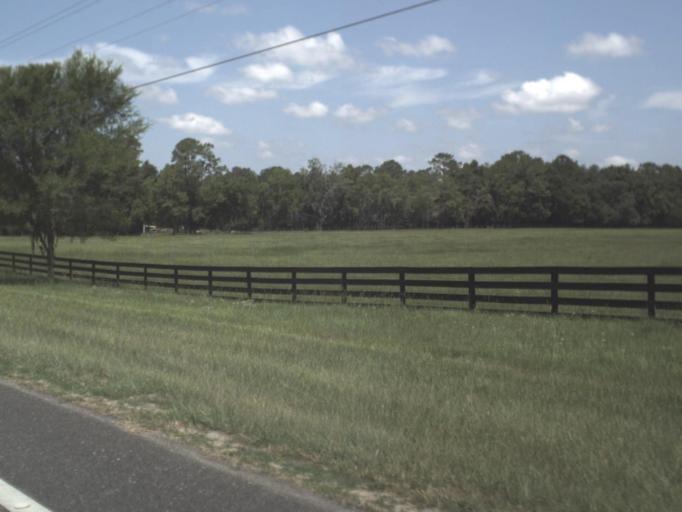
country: US
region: Florida
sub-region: Levy County
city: Williston
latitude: 29.3746
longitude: -82.4850
